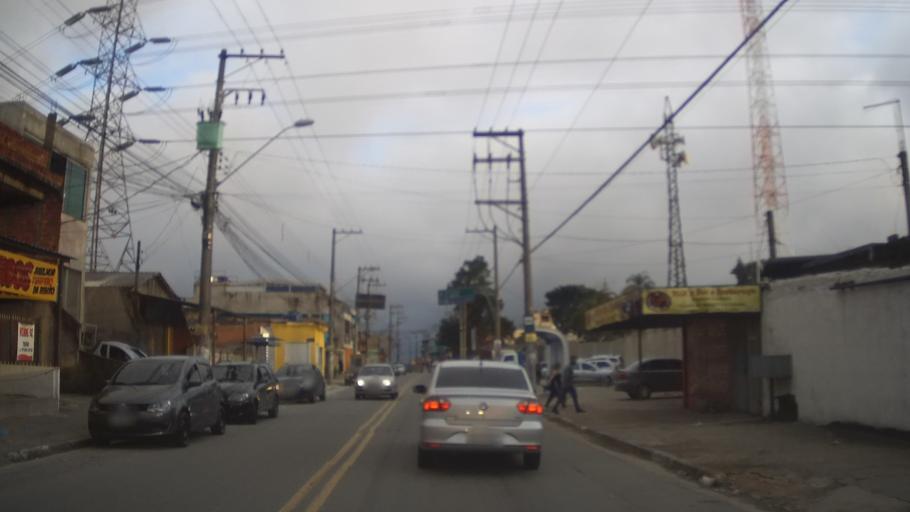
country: BR
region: Sao Paulo
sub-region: Itaquaquecetuba
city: Itaquaquecetuba
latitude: -23.4579
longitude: -46.4227
